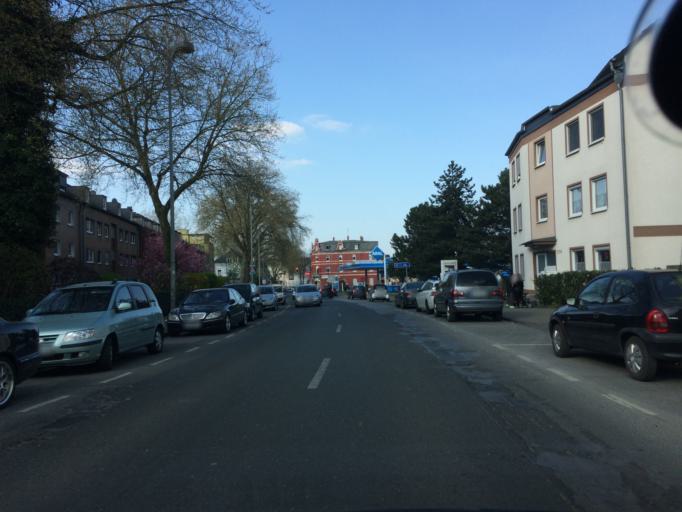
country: DE
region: North Rhine-Westphalia
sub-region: Regierungsbezirk Munster
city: Gelsenkirchen
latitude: 51.5320
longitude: 7.1099
